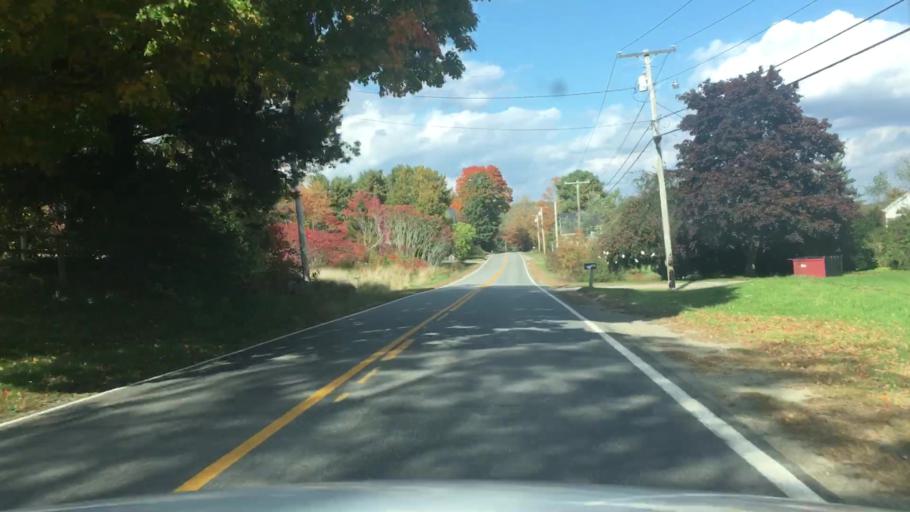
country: US
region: Maine
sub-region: Knox County
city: Union
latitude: 44.2238
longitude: -69.2844
